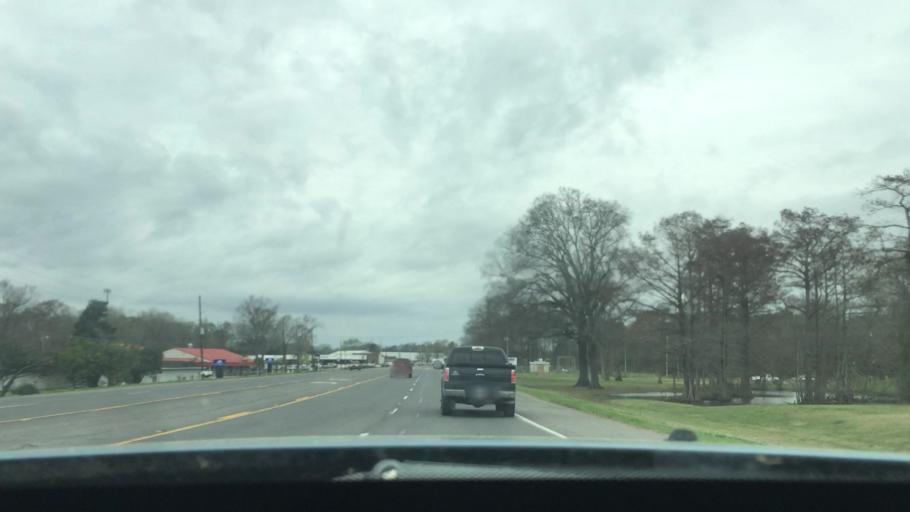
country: US
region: Louisiana
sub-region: Franklin Parish
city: Winnsboro
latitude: 32.1536
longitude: -91.7091
